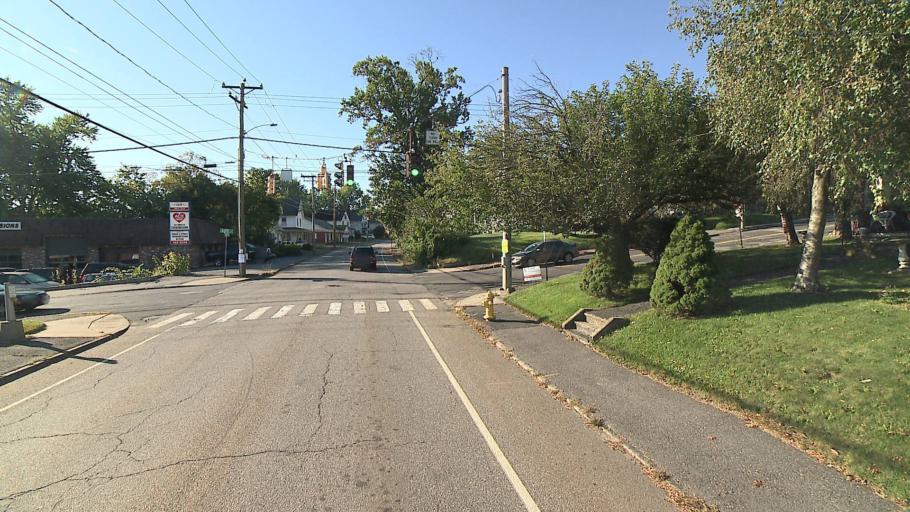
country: US
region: Connecticut
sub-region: Litchfield County
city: Torrington
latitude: 41.7952
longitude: -73.1244
